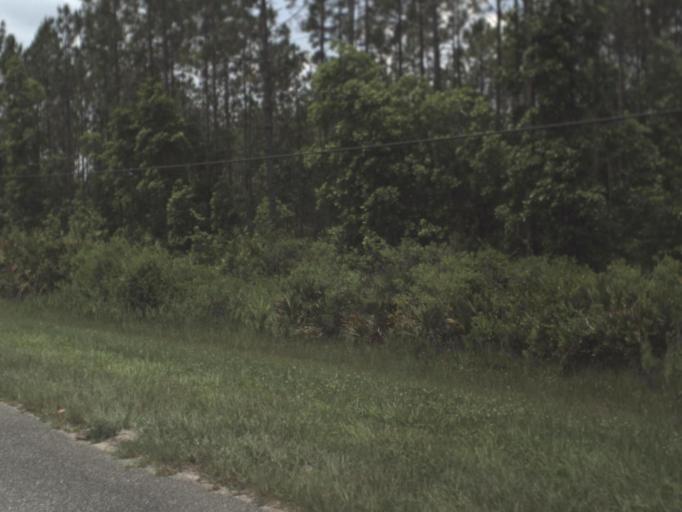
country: US
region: Florida
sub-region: Putnam County
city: Palatka
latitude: 29.5786
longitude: -81.7189
